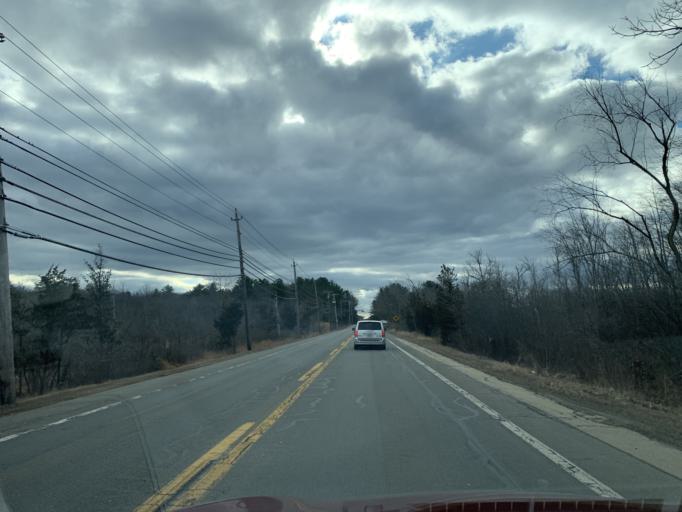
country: US
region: Massachusetts
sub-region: Essex County
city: Newburyport
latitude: 42.7774
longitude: -70.8840
